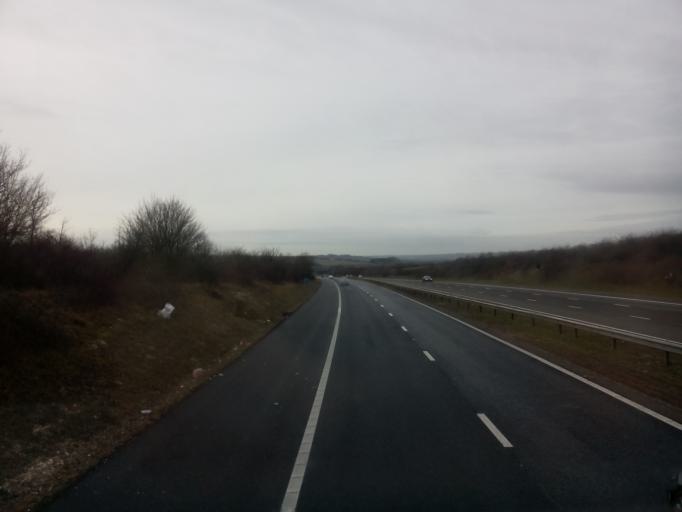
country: GB
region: England
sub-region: Hampshire
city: Kings Worthy
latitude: 51.1044
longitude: -1.2706
